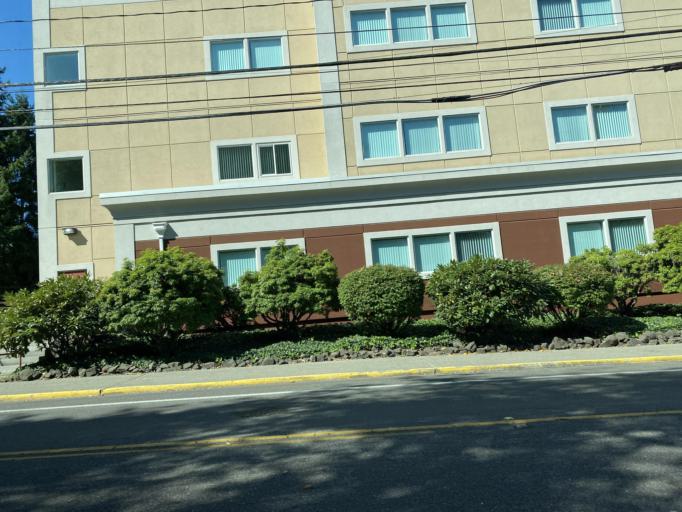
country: US
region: Washington
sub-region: Thurston County
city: Olympia
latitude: 47.0372
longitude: -122.8872
